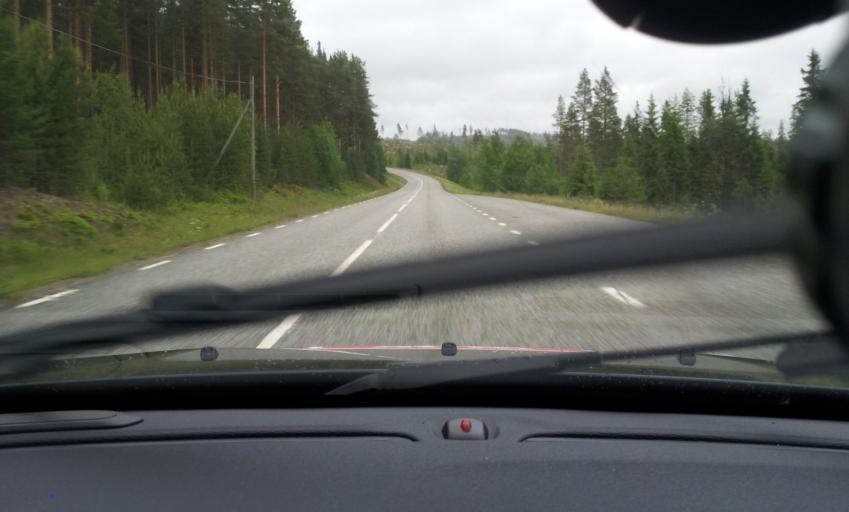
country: SE
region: Jaemtland
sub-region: Stroemsunds Kommun
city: Stroemsund
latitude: 63.3455
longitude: 15.7406
